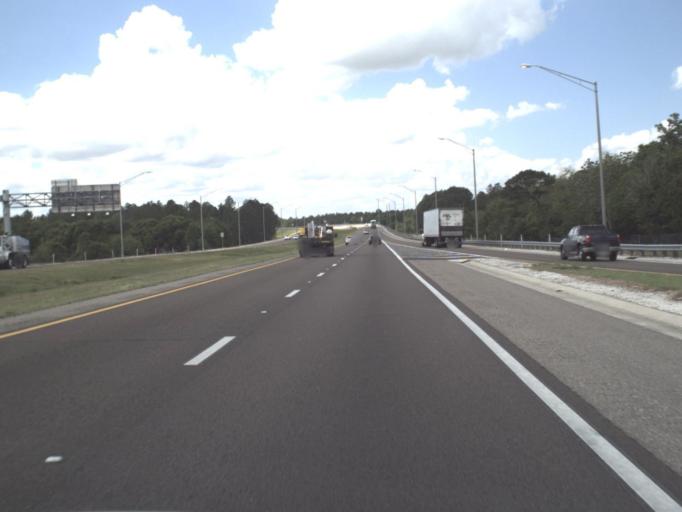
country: US
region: Florida
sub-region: Orange County
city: Paradise Heights
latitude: 28.6003
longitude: -81.5474
